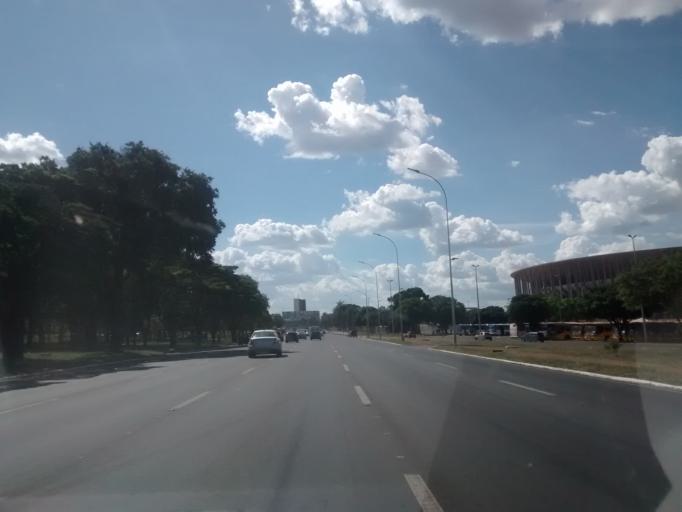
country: BR
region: Federal District
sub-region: Brasilia
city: Brasilia
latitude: -15.7880
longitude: -47.8955
